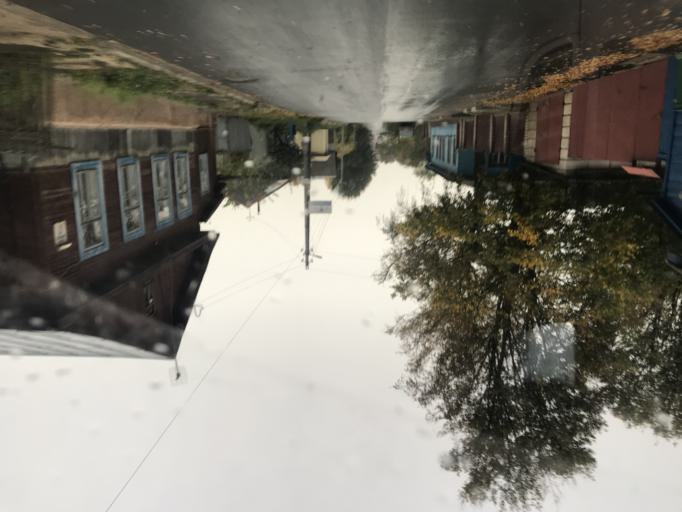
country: BY
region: Mogilev
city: Mahilyow
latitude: 53.8976
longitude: 30.3231
